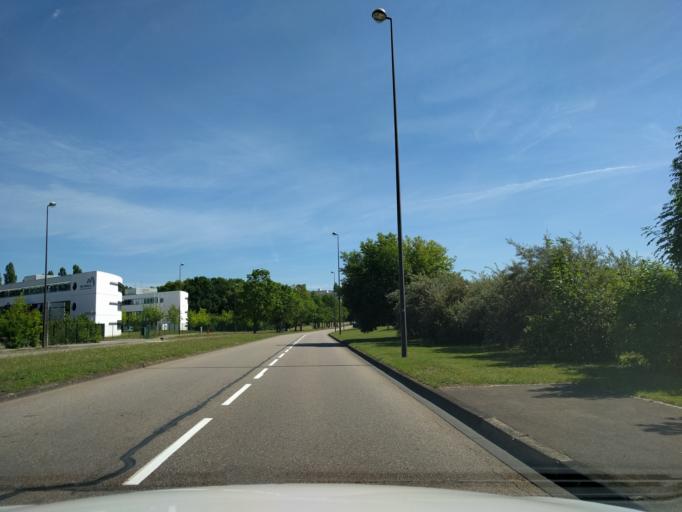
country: FR
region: Lorraine
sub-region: Departement de la Moselle
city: Saint-Julien-les-Metz
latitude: 49.1049
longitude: 6.2150
